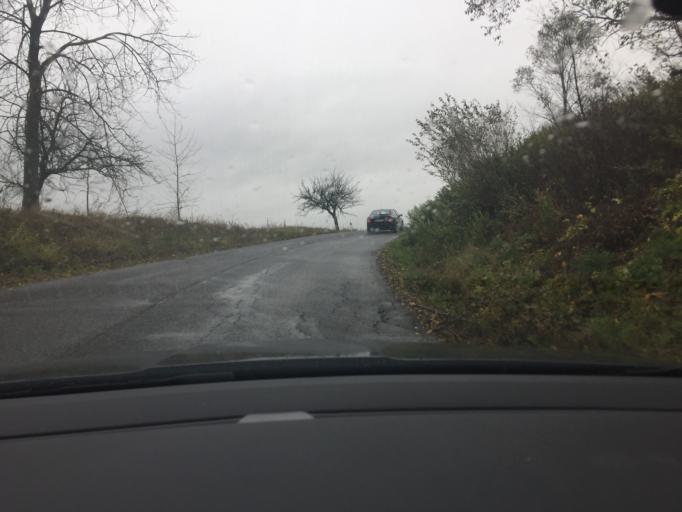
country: SK
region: Presovsky
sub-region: Okres Presov
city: Kezmarok
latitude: 49.1670
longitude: 20.4149
